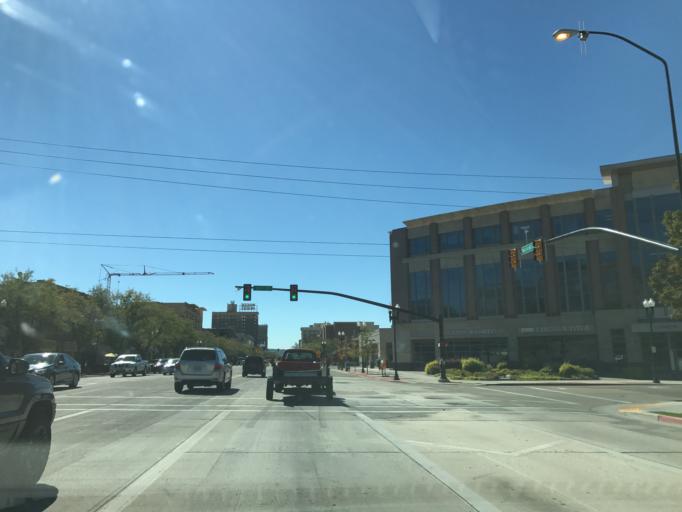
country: US
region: Utah
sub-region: Weber County
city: Ogden
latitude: 41.2272
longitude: -111.9704
